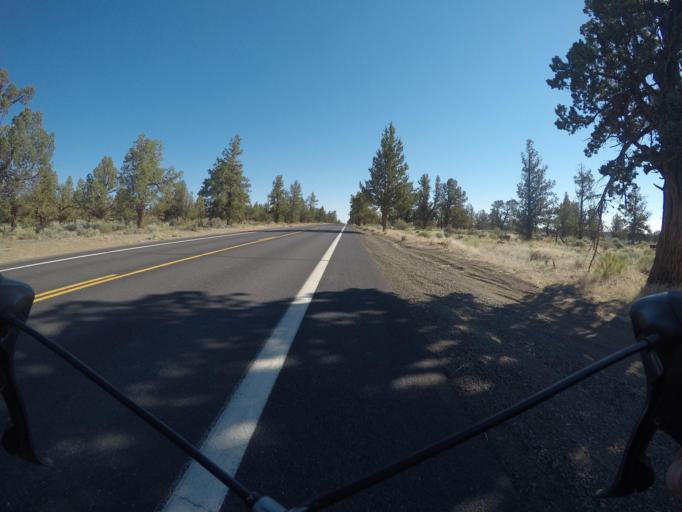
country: US
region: Oregon
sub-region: Deschutes County
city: Redmond
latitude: 44.2147
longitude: -121.3155
